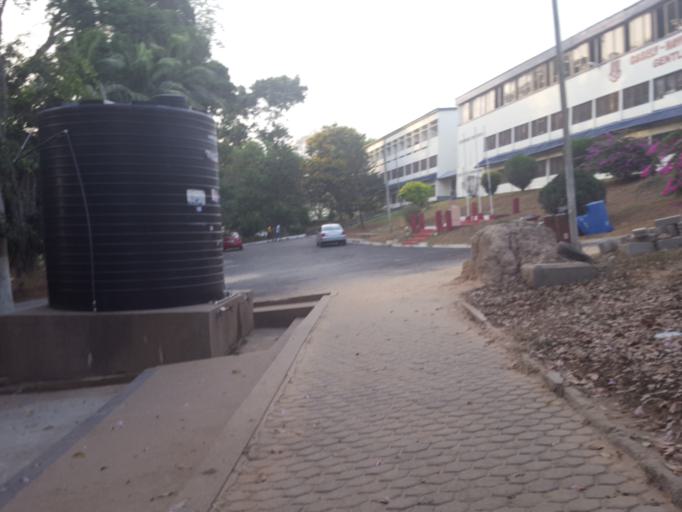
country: GH
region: Central
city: Cape Coast
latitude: 5.1163
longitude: -1.2836
